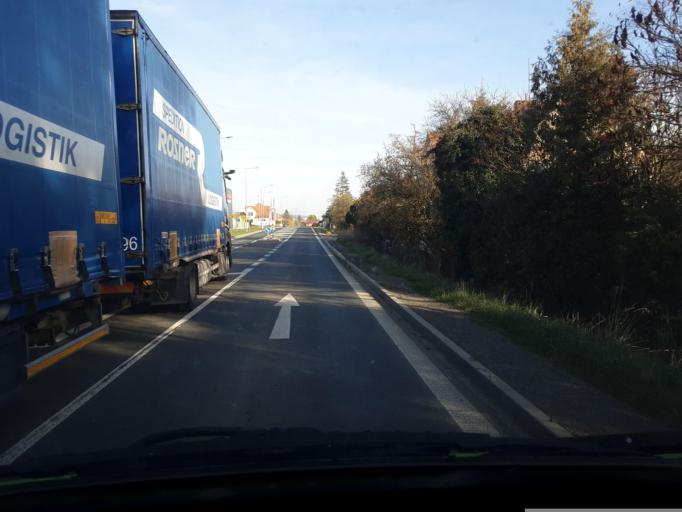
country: CZ
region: Plzensky
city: Horazd'ovice
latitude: 49.3244
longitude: 13.6847
